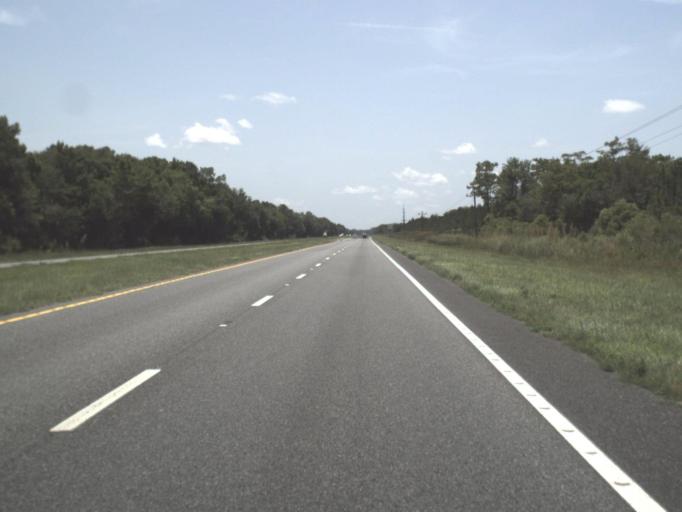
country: US
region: Florida
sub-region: Taylor County
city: Steinhatchee
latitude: 29.8031
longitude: -83.3403
